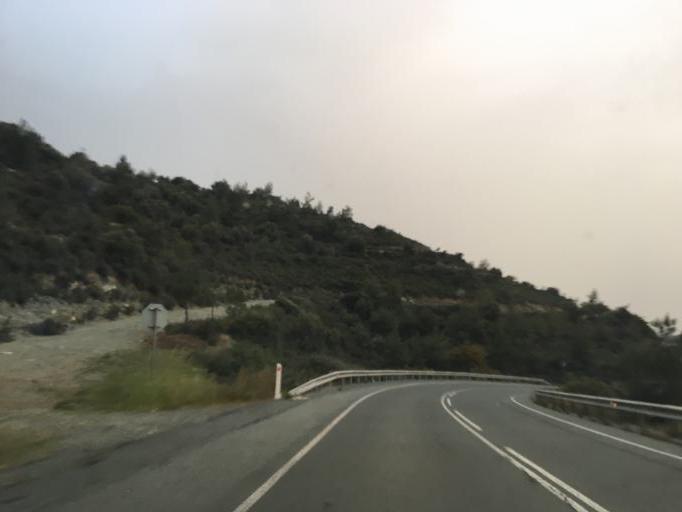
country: CY
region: Limassol
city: Parekklisha
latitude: 34.7995
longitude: 33.1519
